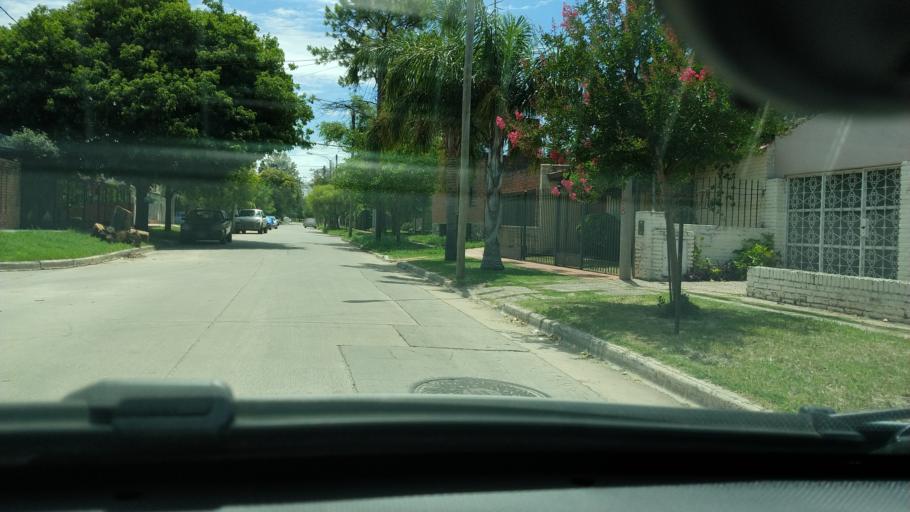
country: AR
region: Cordoba
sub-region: Departamento de Capital
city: Cordoba
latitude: -31.3604
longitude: -64.2309
